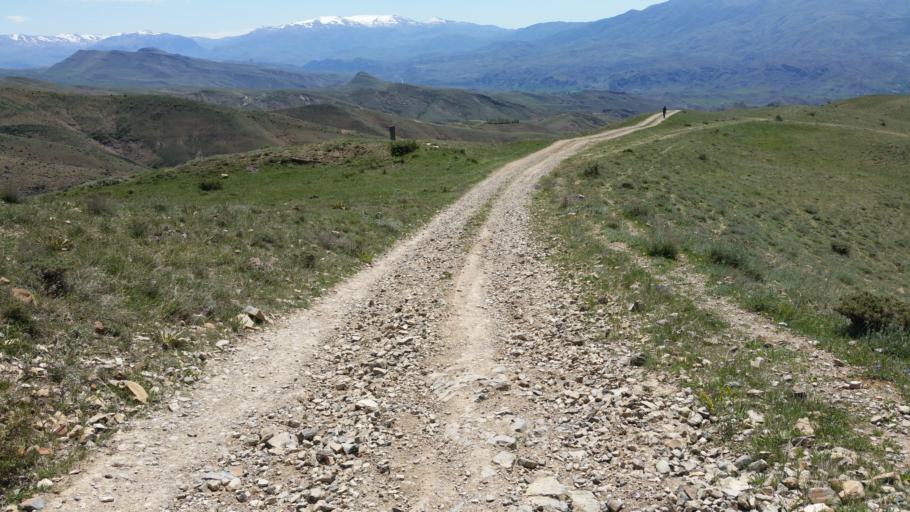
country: AM
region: Vayots' Dzori Marz
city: Vernashen
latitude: 39.8027
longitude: 45.3602
